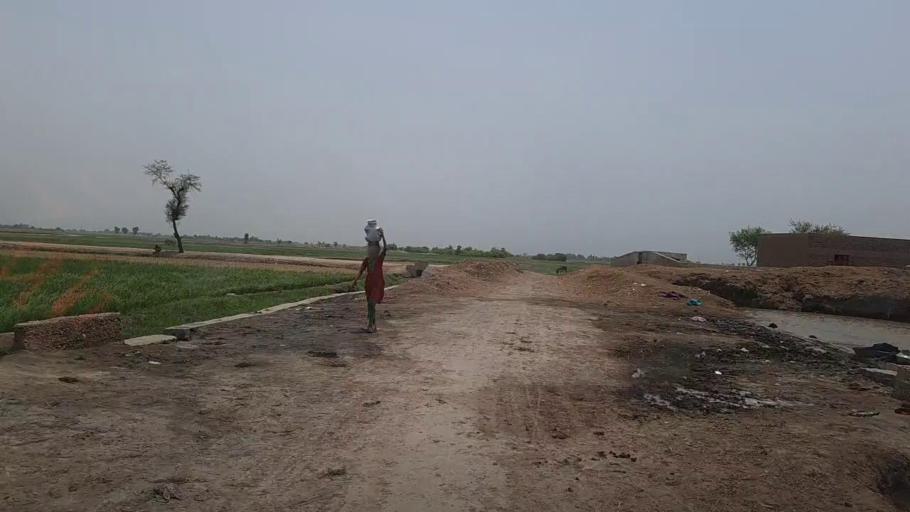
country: PK
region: Sindh
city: Sita Road
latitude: 27.0710
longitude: 67.8516
